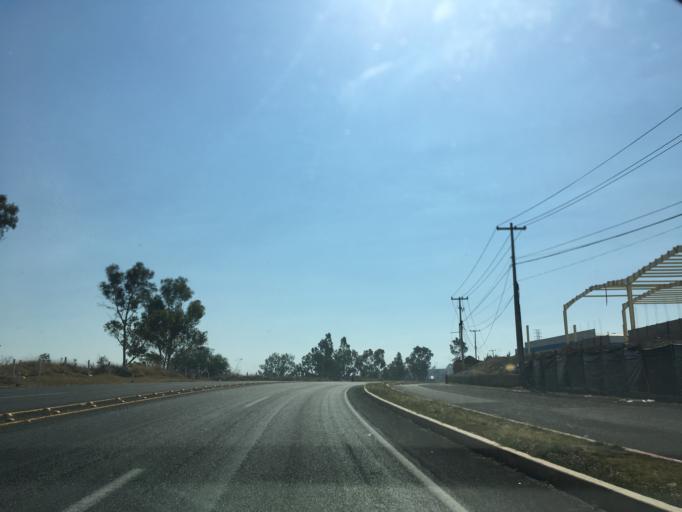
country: MX
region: Michoacan
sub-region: Morelia
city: La Aldea
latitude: 19.7343
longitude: -101.1294
